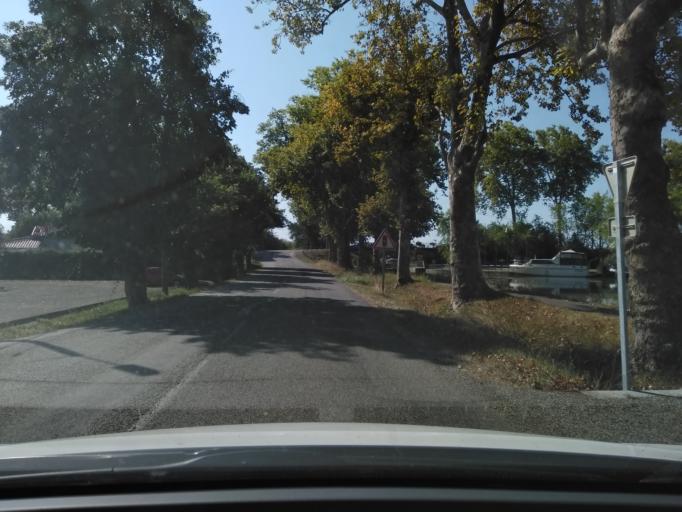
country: FR
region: Midi-Pyrenees
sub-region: Departement du Tarn-et-Garonne
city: Montech
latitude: 43.9608
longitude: 1.2371
